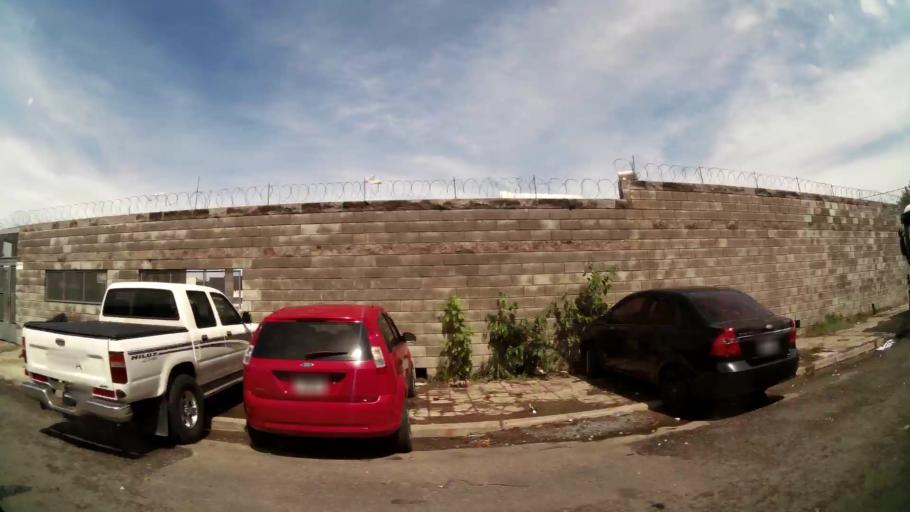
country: AR
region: Buenos Aires F.D.
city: Villa Lugano
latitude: -34.6671
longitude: -58.4375
